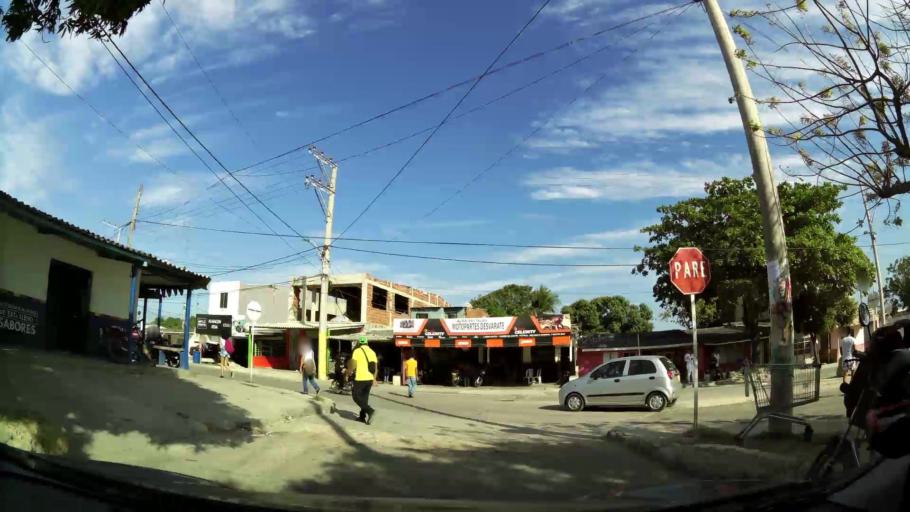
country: CO
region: Atlantico
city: Soledad
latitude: 10.9246
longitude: -74.8152
